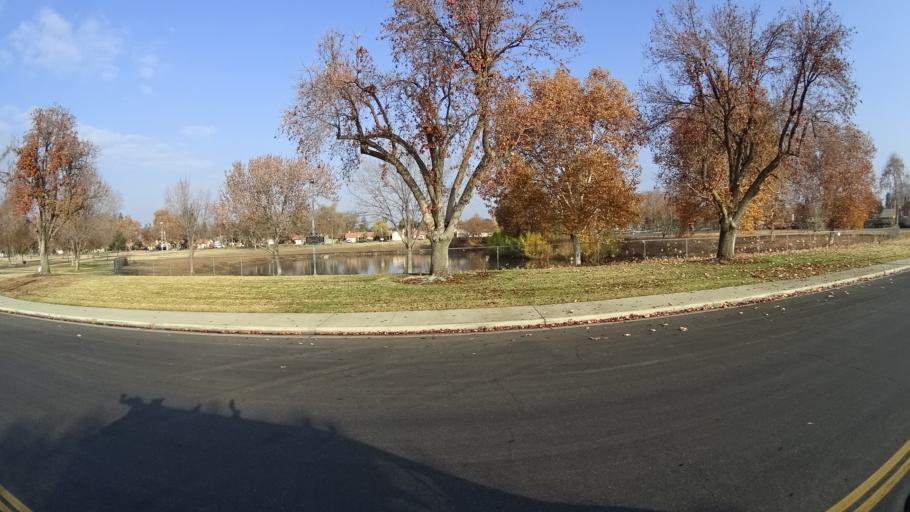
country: US
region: California
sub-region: Kern County
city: Greenacres
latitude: 35.3137
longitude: -119.0999
